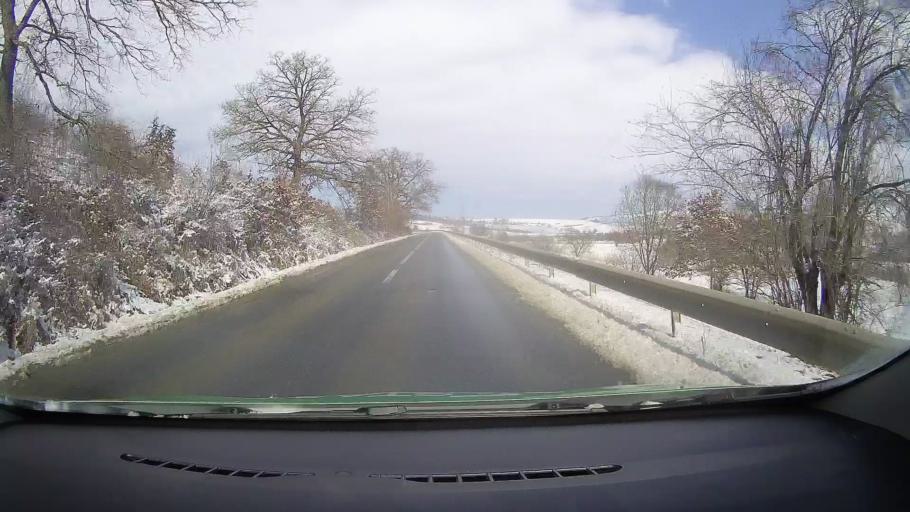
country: RO
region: Sibiu
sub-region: Comuna Altina
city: Altina
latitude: 45.9534
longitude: 24.4533
